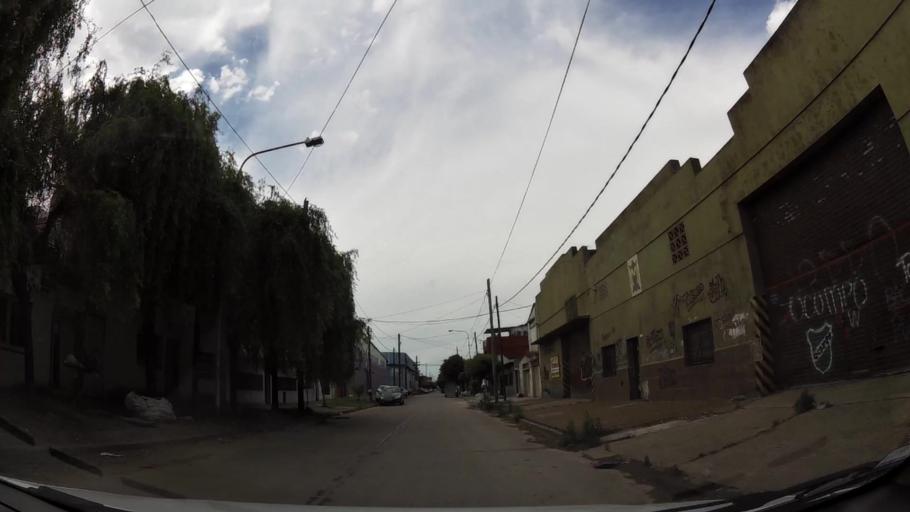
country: AR
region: Buenos Aires
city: San Justo
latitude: -34.6876
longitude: -58.5434
